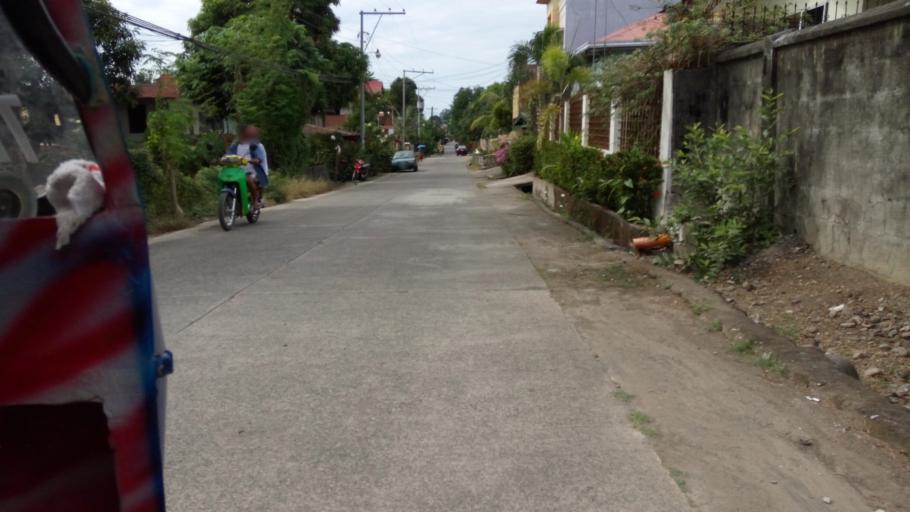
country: PH
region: Ilocos
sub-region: Province of La Union
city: Aringay
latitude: 16.3927
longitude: 120.3557
